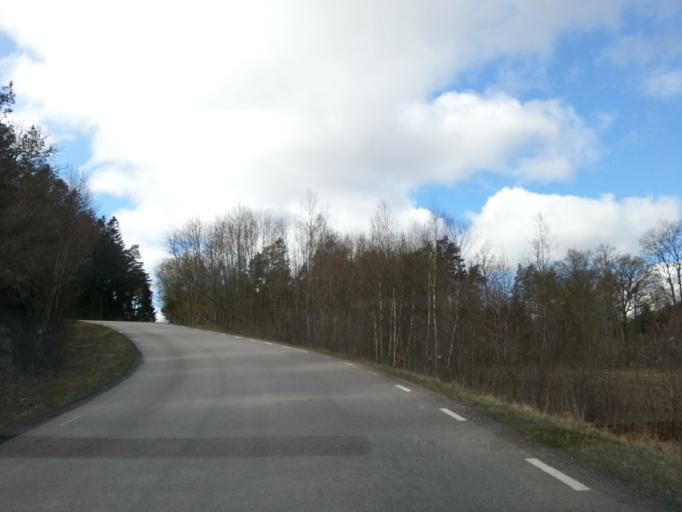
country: SE
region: Vaestra Goetaland
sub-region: Kungalvs Kommun
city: Kode
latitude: 57.8343
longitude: 11.8671
